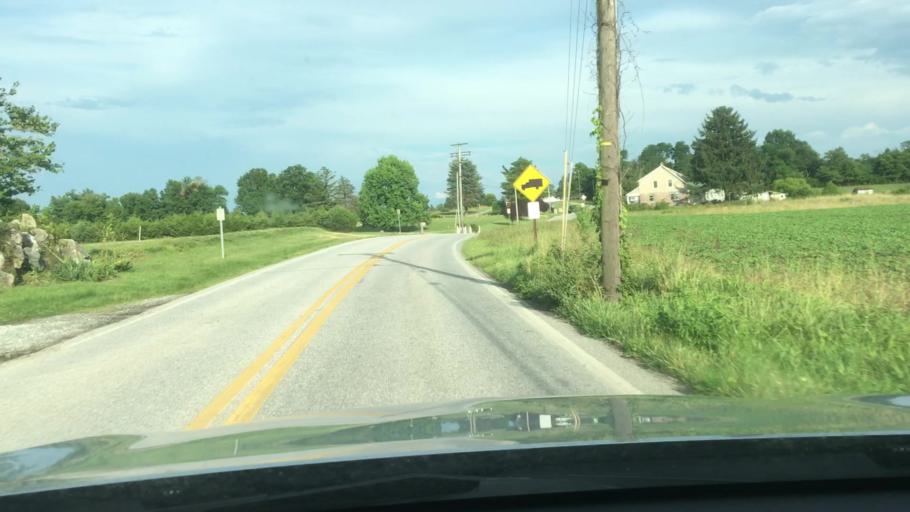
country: US
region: Pennsylvania
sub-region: York County
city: Dover
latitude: 40.0210
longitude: -76.8194
